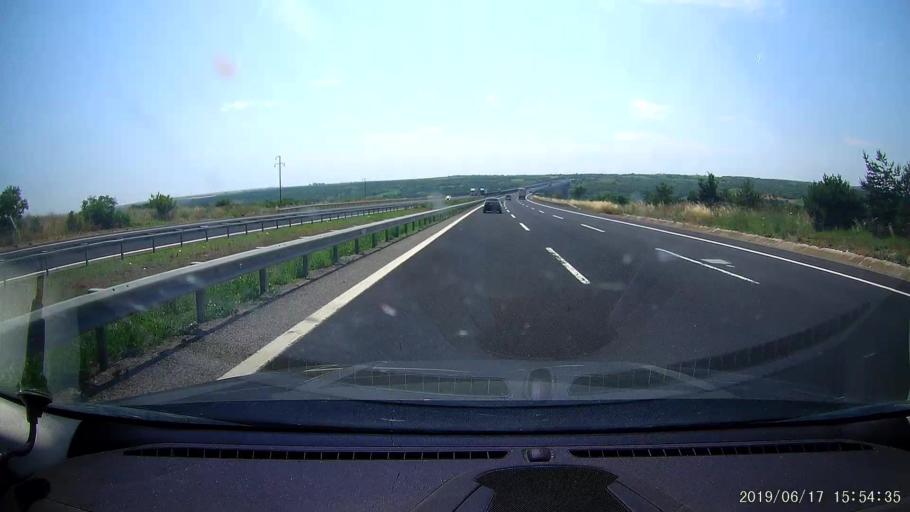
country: TR
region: Istanbul
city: Buyukcavuslu
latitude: 41.1975
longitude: 28.0402
